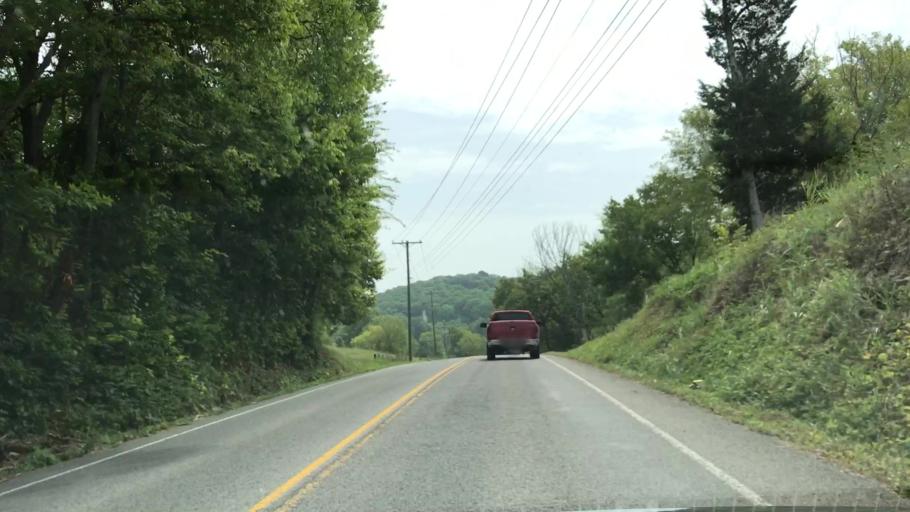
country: US
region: Tennessee
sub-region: Williamson County
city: Nolensville
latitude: 35.9263
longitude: -86.7282
